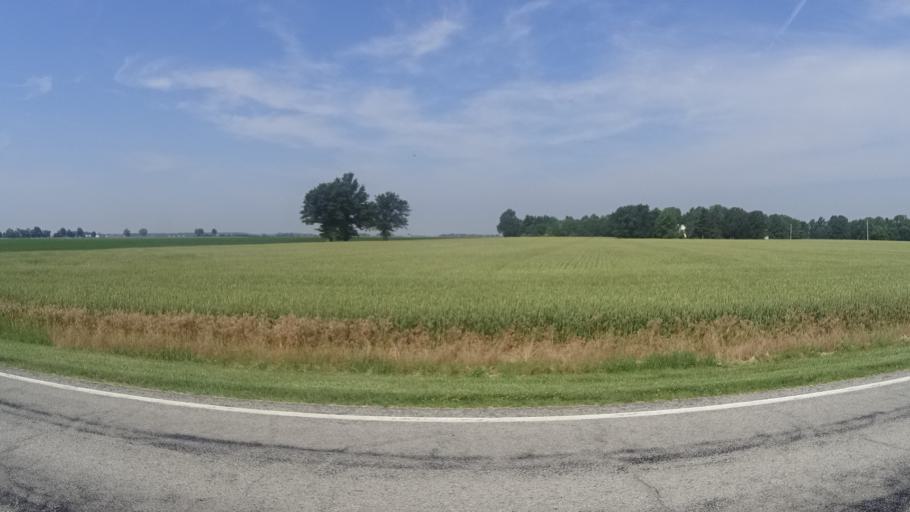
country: US
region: Ohio
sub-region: Huron County
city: Monroeville
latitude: 41.3124
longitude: -82.7145
